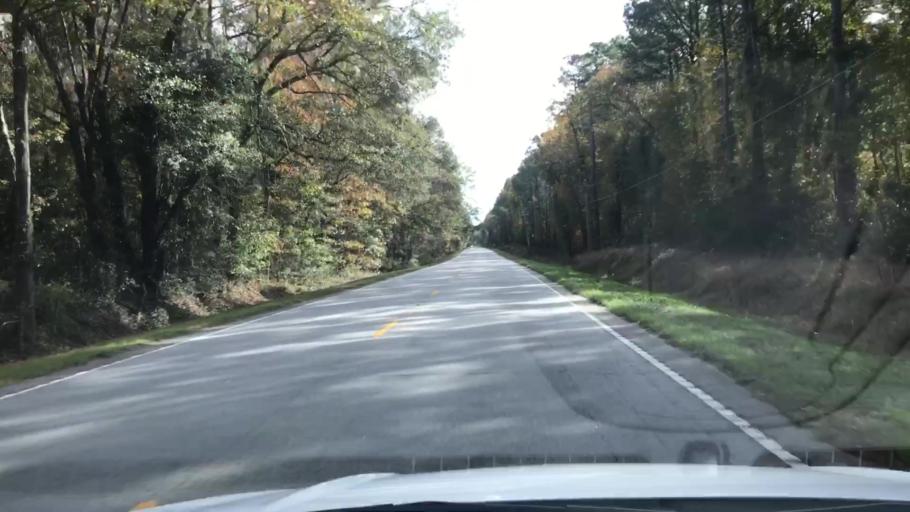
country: US
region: South Carolina
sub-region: Colleton County
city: Walterboro
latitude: 32.8007
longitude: -80.5017
